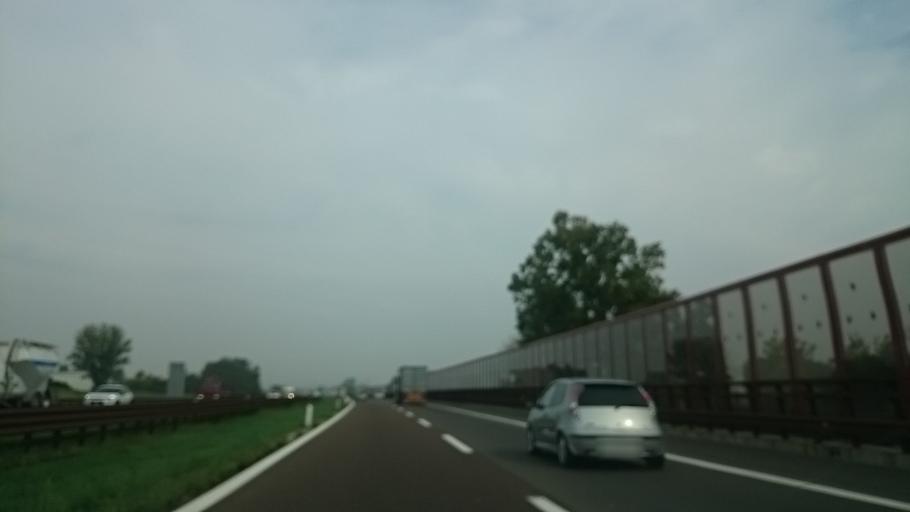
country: IT
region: Emilia-Romagna
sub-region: Provincia di Modena
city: Campogalliano
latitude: 44.6932
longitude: 10.8510
